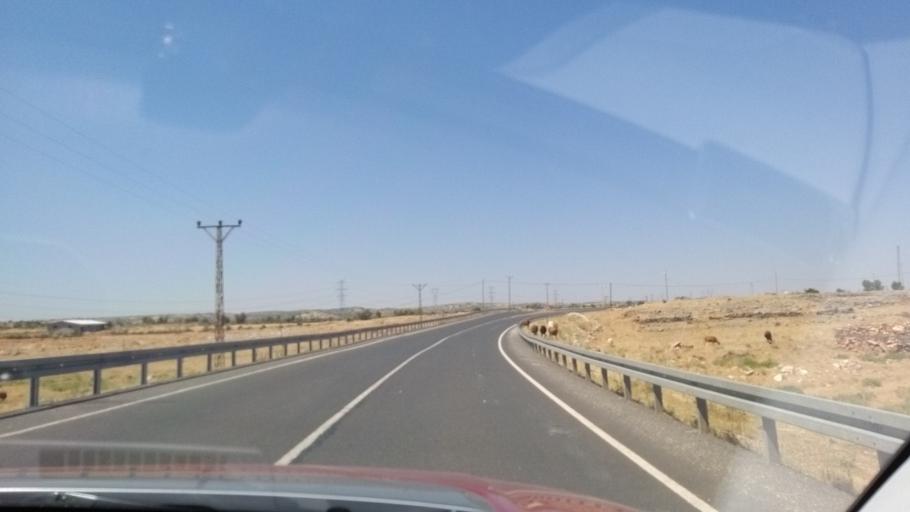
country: TR
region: Mardin
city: Dargecit
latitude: 37.5352
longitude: 41.7318
